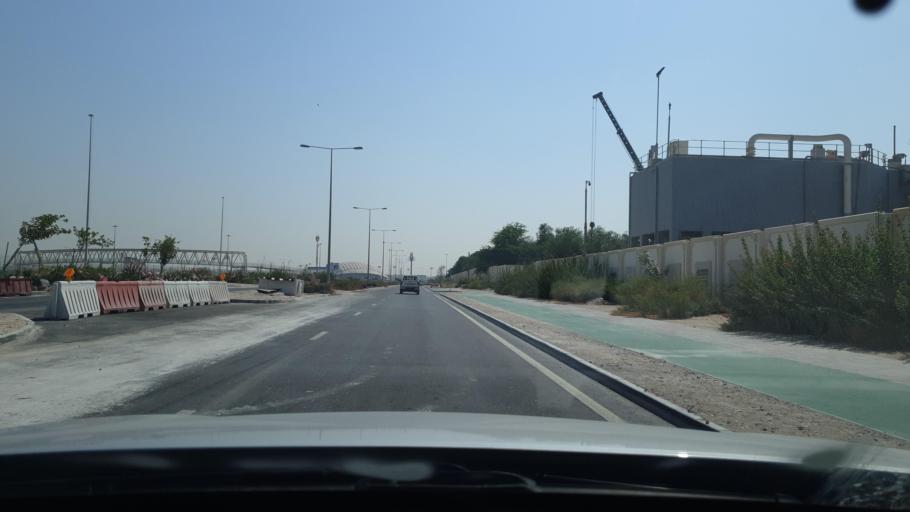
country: QA
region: Baladiyat ad Dawhah
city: Doha
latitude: 25.2313
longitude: 51.5262
